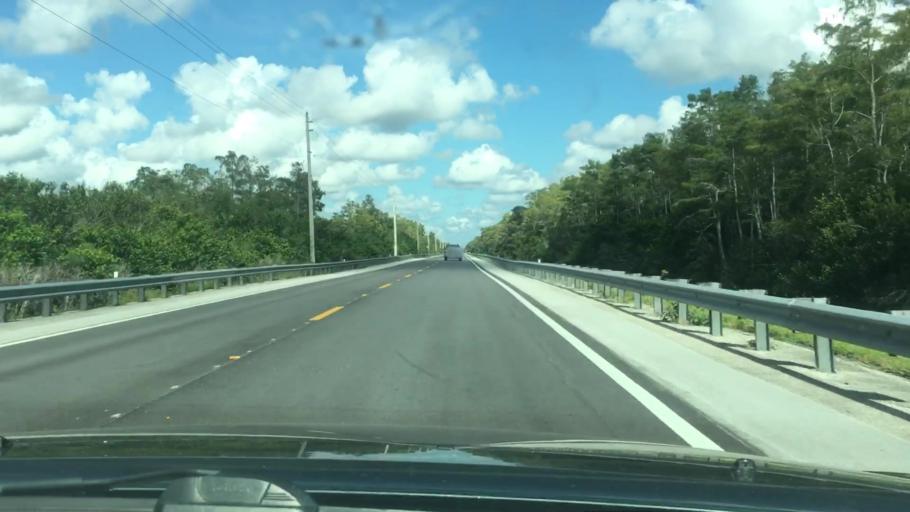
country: US
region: Florida
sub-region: Miami-Dade County
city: Kendall West
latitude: 25.7661
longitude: -80.8326
